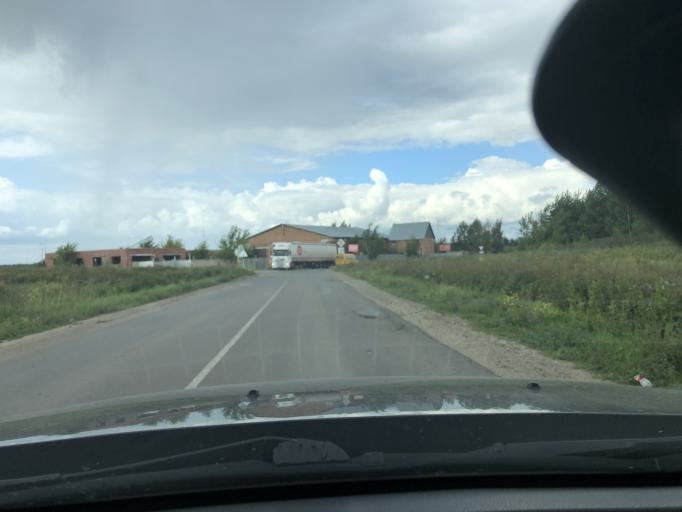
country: RU
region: Tula
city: Kamenetskiy
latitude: 54.0166
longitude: 38.2523
